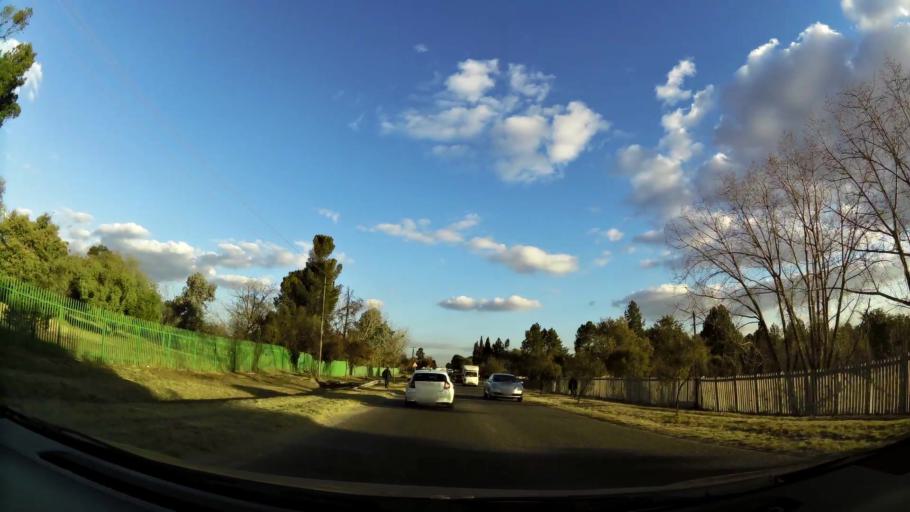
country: ZA
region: Gauteng
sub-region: City of Johannesburg Metropolitan Municipality
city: Midrand
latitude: -25.9636
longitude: 28.1537
